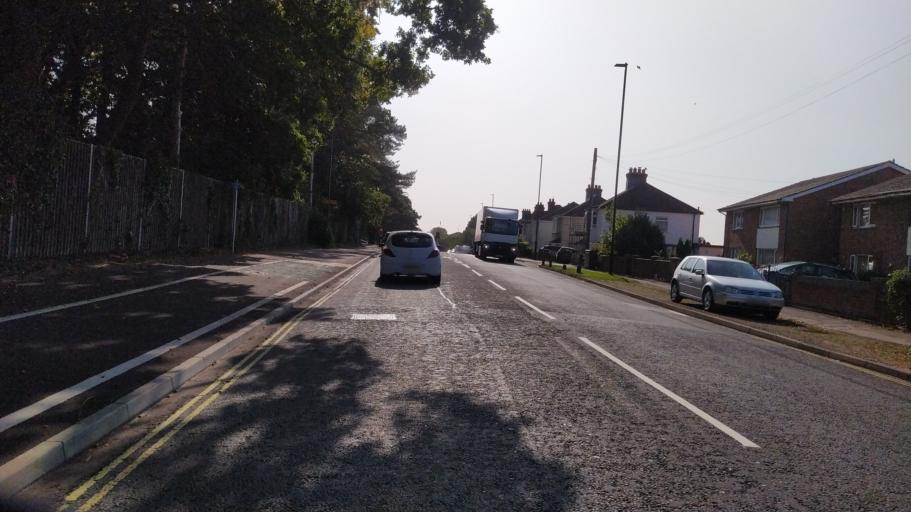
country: GB
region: England
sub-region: Hampshire
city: West End
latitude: 50.9078
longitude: -1.3447
